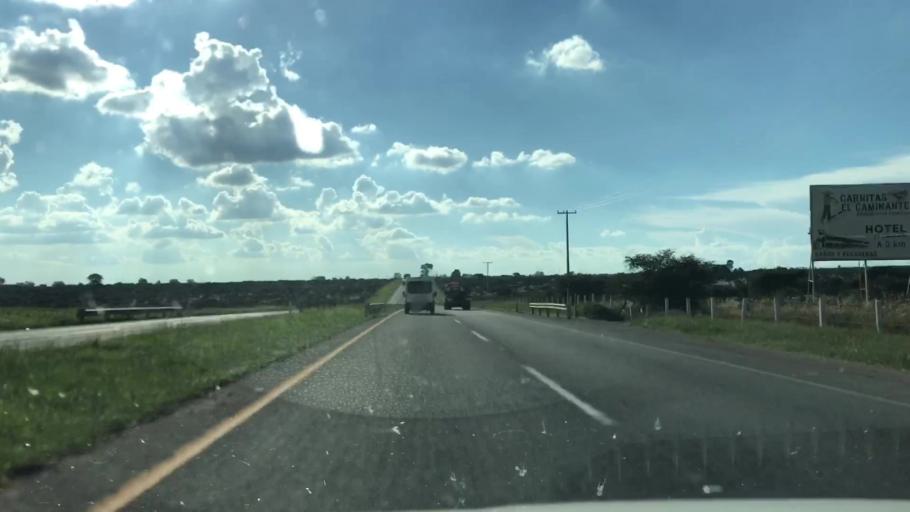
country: MX
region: Jalisco
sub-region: Lagos de Moreno
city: Cristeros [Fraccionamiento]
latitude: 21.3048
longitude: -102.0937
